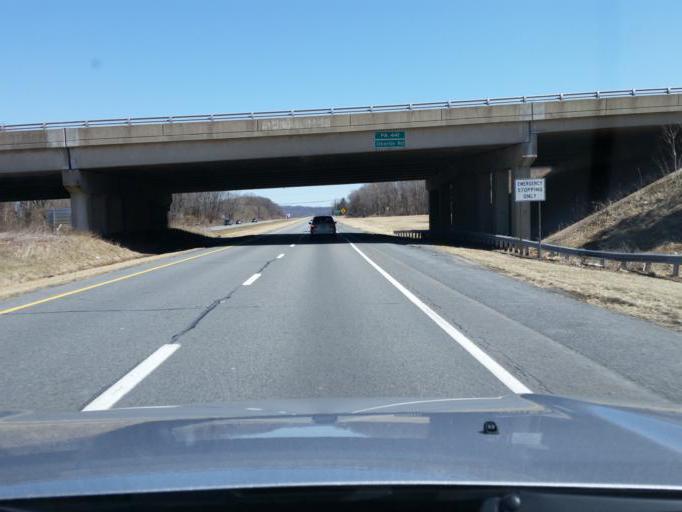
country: US
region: Pennsylvania
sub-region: Dauphin County
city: Highspire
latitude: 40.2252
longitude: -76.7583
